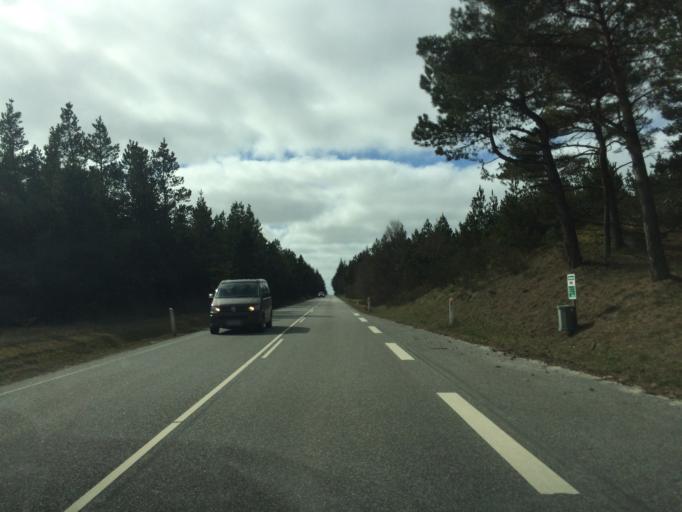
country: DK
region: Central Jutland
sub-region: Holstebro Kommune
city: Ulfborg
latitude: 56.2890
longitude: 8.1846
